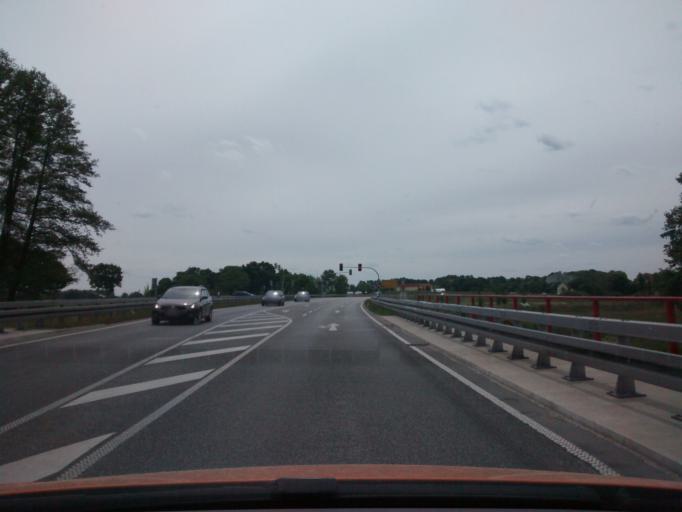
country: DE
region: Brandenburg
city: Juterbog
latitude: 52.0349
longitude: 13.1073
